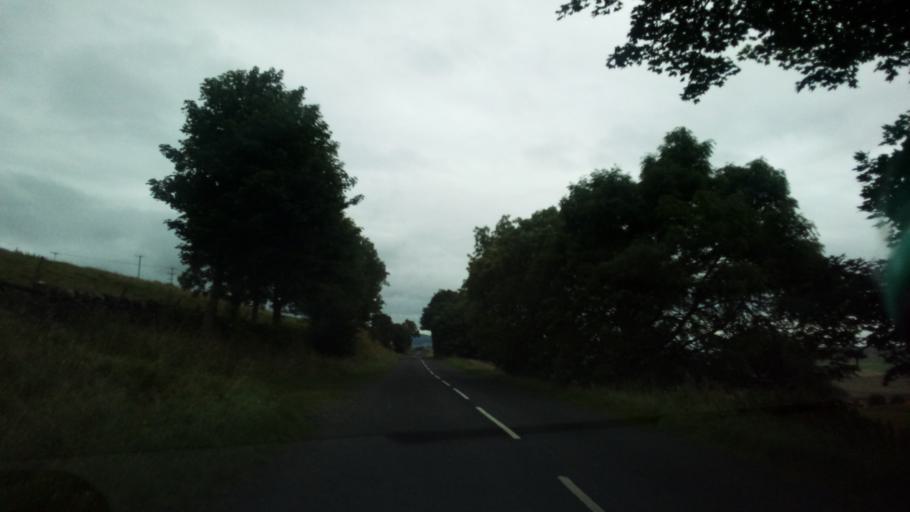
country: GB
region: England
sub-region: County Durham
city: Holwick
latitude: 54.5939
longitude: -2.1288
